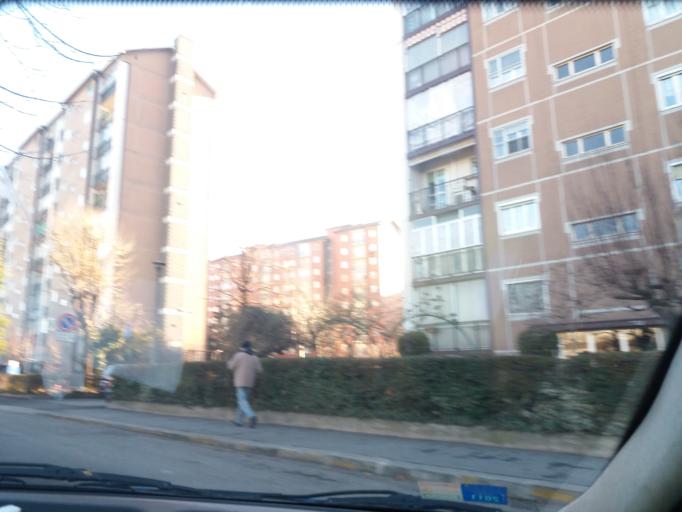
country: IT
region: Piedmont
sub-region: Provincia di Torino
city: Fornaci
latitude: 45.0199
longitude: 7.6163
